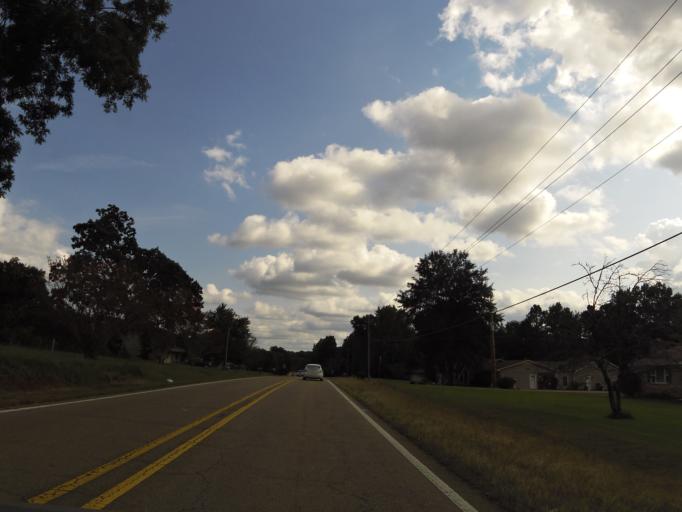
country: US
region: Mississippi
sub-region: Alcorn County
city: Farmington
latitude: 34.9877
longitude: -88.4625
